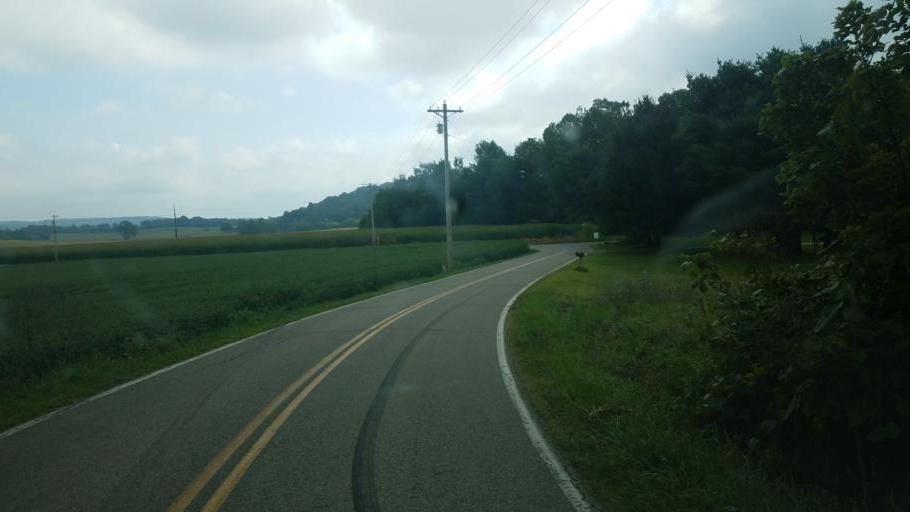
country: US
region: Ohio
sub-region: Licking County
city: Utica
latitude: 40.1986
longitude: -82.4701
